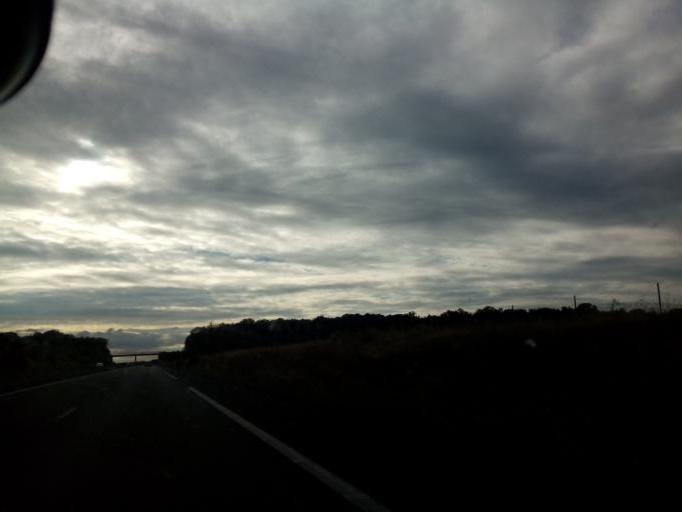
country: FR
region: Centre
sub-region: Departement d'Indre-et-Loire
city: Monts
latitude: 47.3074
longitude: 0.6206
